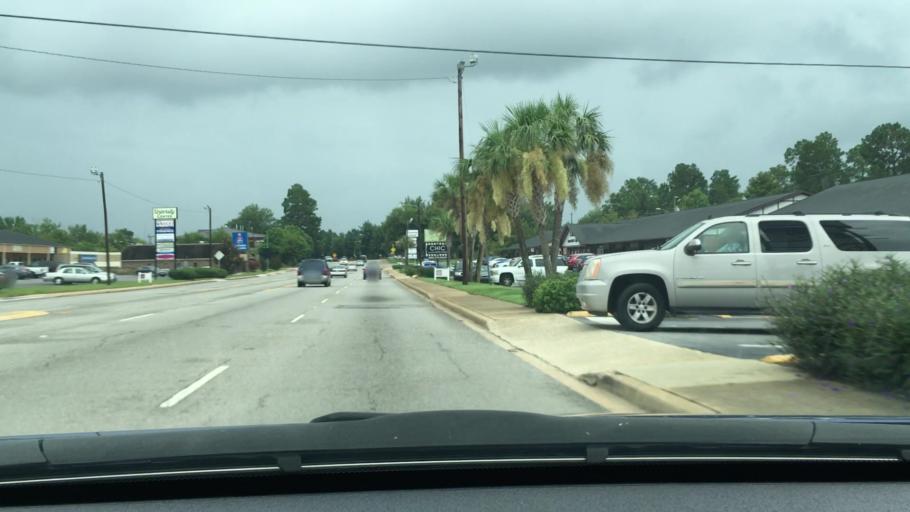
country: US
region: South Carolina
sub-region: Sumter County
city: Sumter
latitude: 33.9378
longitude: -80.3714
